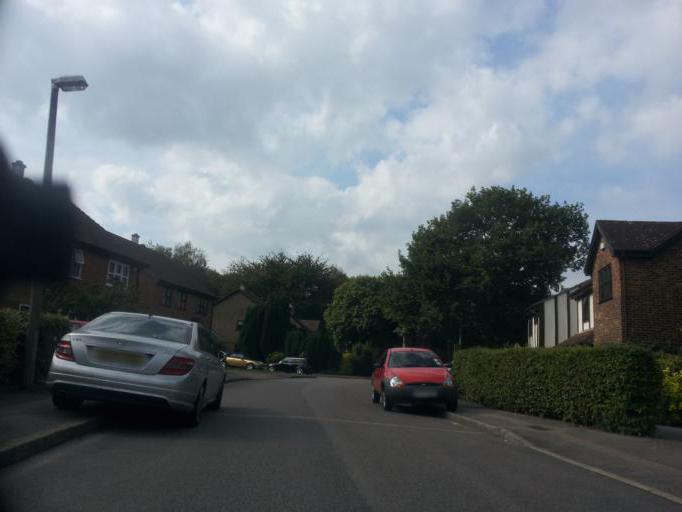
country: GB
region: England
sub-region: Kent
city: Rainham
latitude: 51.3430
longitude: 0.5688
